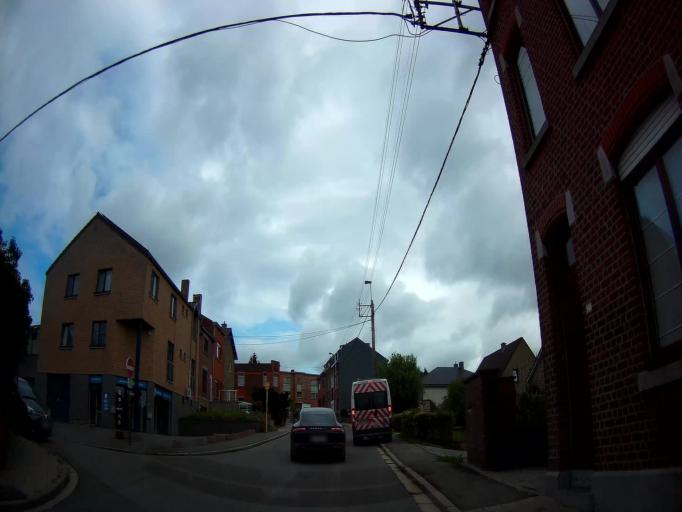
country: BE
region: Wallonia
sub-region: Province de Liege
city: Chaudfontaine
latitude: 50.6189
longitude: 5.6251
